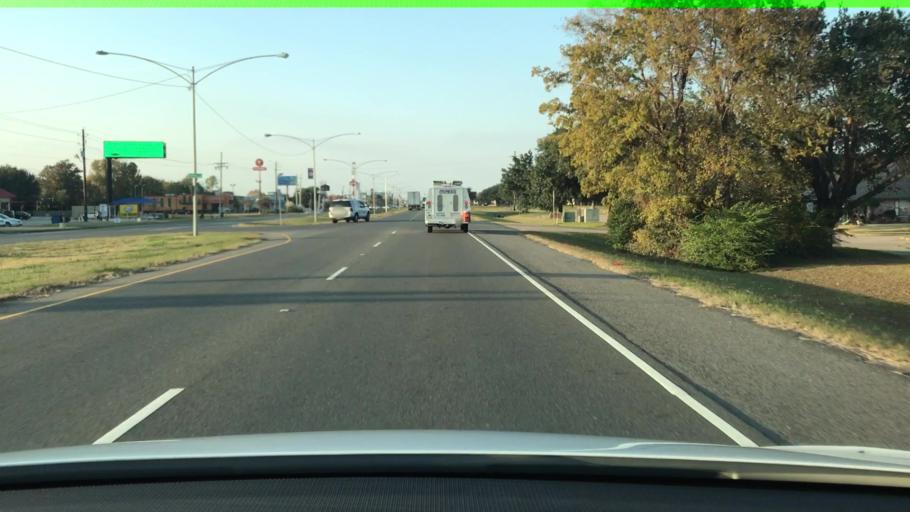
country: US
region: Louisiana
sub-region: Bossier Parish
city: Bossier City
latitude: 32.4234
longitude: -93.7069
